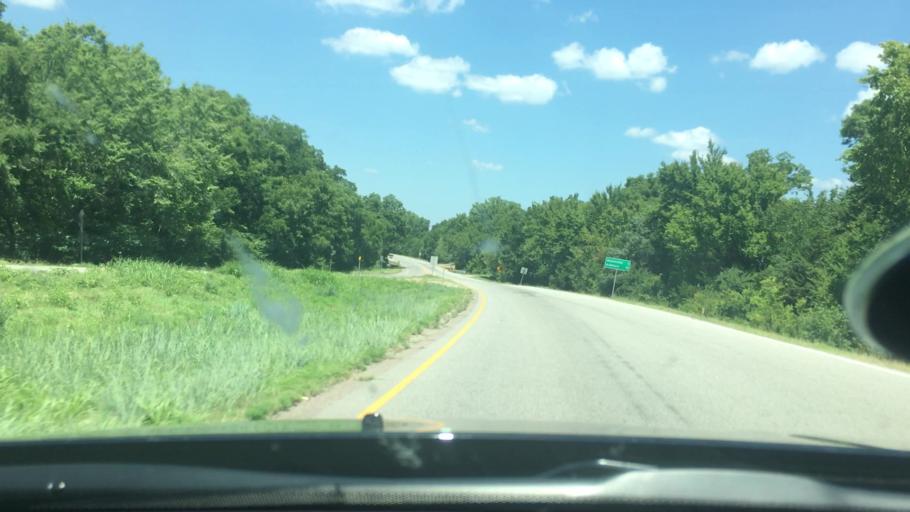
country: US
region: Oklahoma
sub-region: Marshall County
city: Oakland
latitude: 34.1708
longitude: -96.8349
